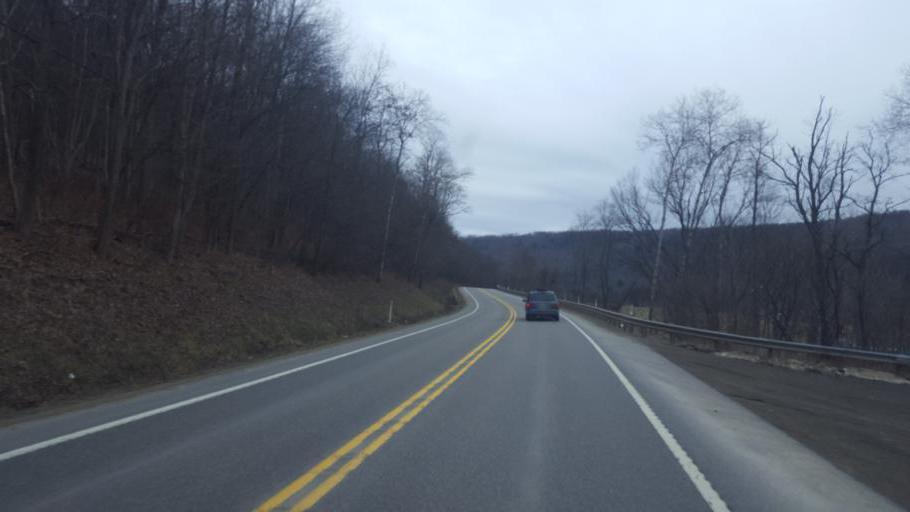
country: US
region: Pennsylvania
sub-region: Potter County
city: Coudersport
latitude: 41.7475
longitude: -78.0936
